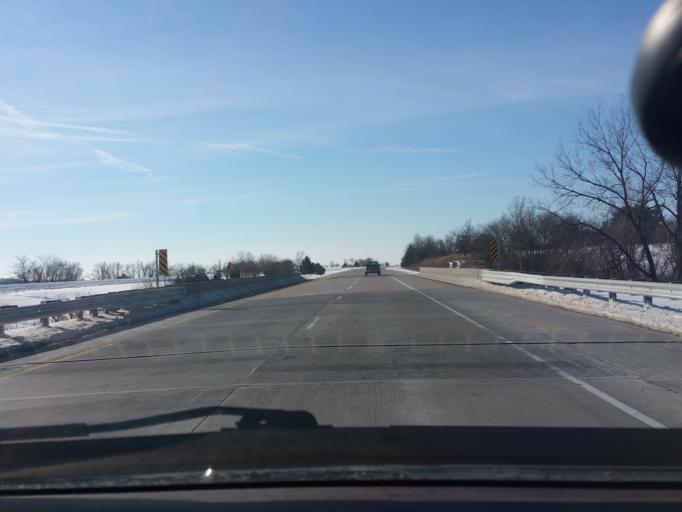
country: US
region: Iowa
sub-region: Decatur County
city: Lamoni
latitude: 40.5951
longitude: -93.9172
